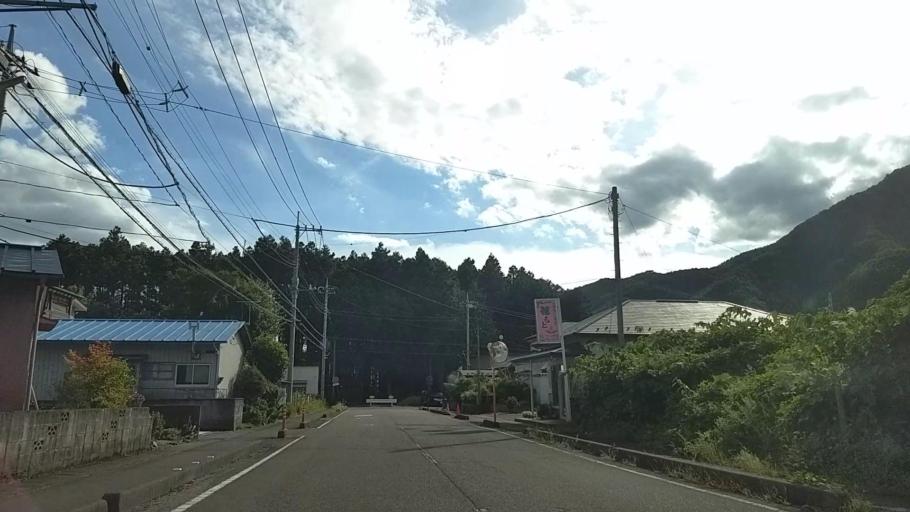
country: JP
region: Tochigi
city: Imaichi
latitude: 36.8191
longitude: 139.7115
